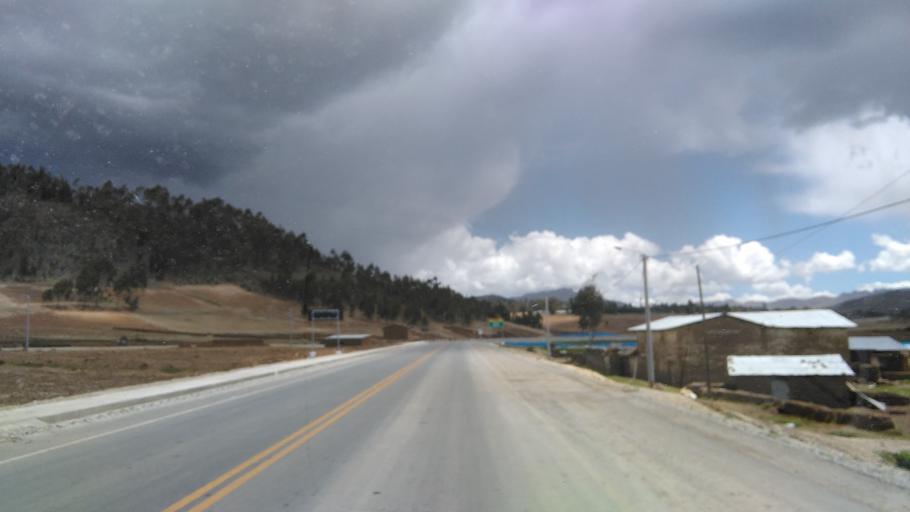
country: PE
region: Apurimac
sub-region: Provincia de Andahuaylas
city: San Jeronimo
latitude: -13.7153
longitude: -73.3499
